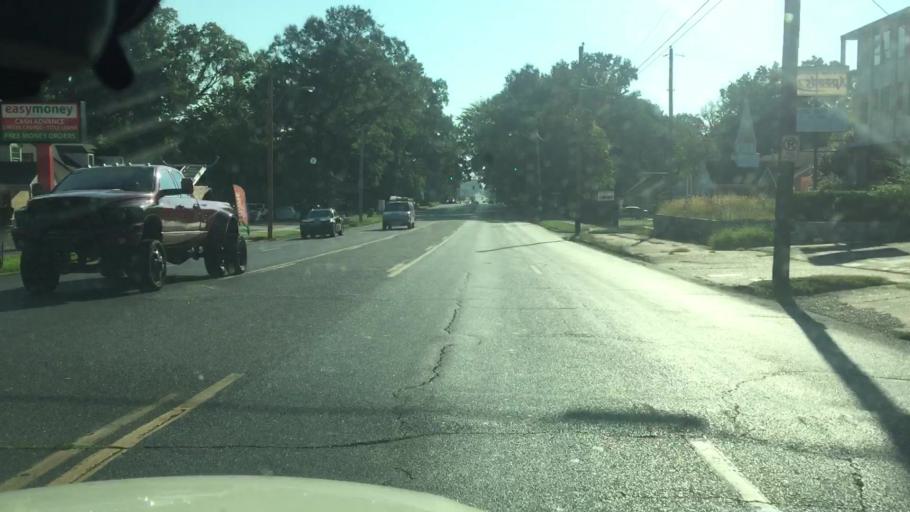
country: US
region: Tennessee
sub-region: Shelby County
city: Memphis
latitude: 35.1077
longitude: -89.9416
